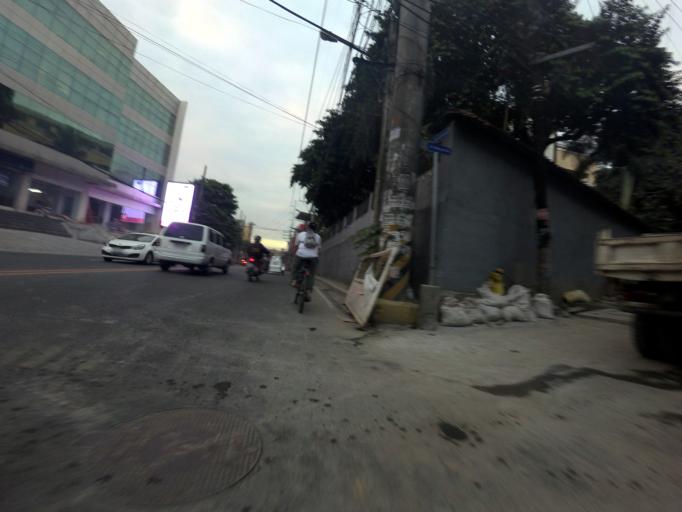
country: PH
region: Metro Manila
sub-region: San Juan
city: San Juan
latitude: 14.6001
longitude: 121.0282
